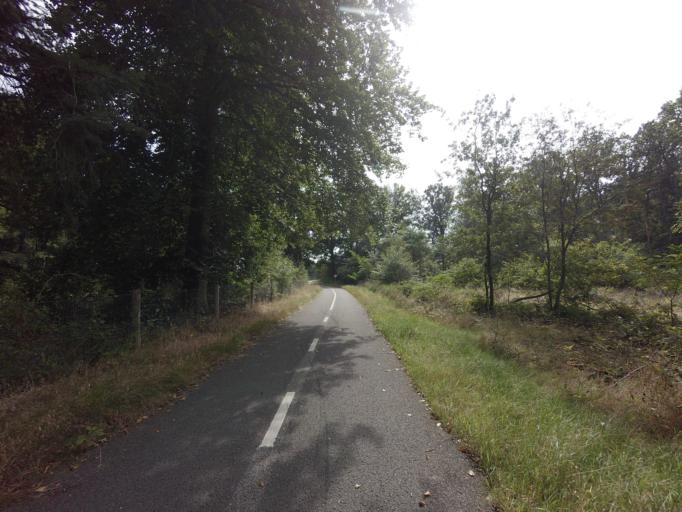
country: NL
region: Drenthe
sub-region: Gemeente Borger-Odoorn
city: Borger
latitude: 52.8820
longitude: 6.7181
